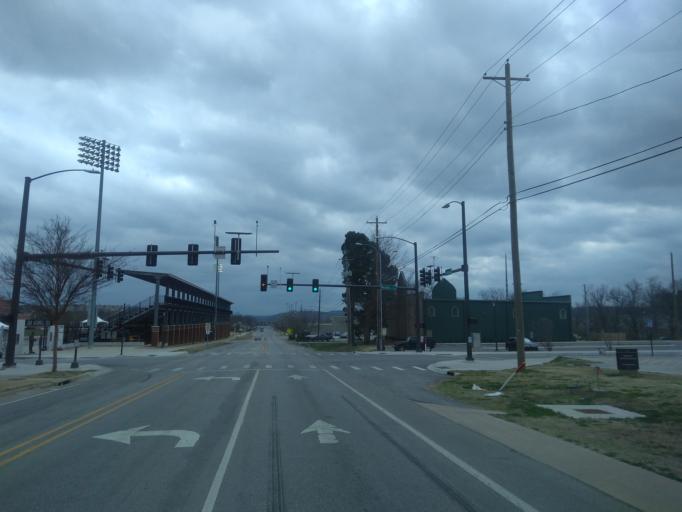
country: US
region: Arkansas
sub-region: Washington County
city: Fayetteville
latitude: 36.0643
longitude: -94.1802
